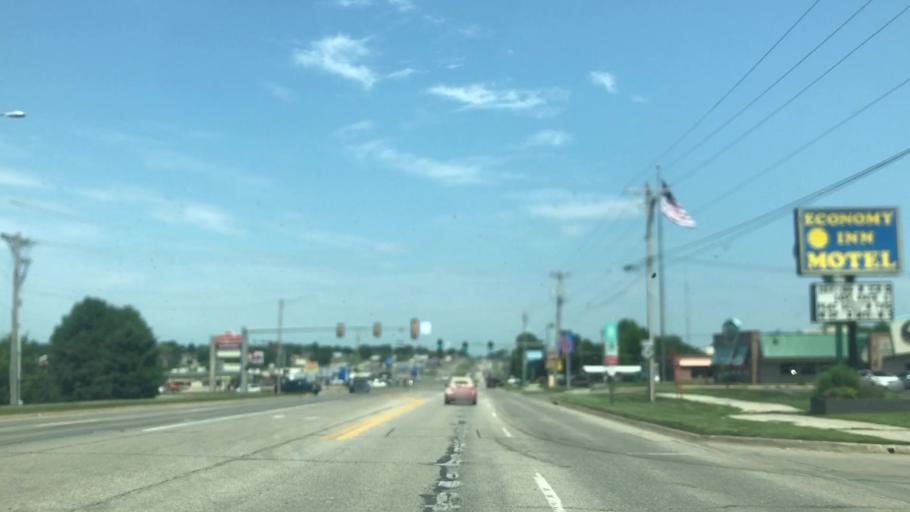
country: US
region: Iowa
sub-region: Marshall County
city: Marshalltown
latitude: 42.0077
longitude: -92.9123
